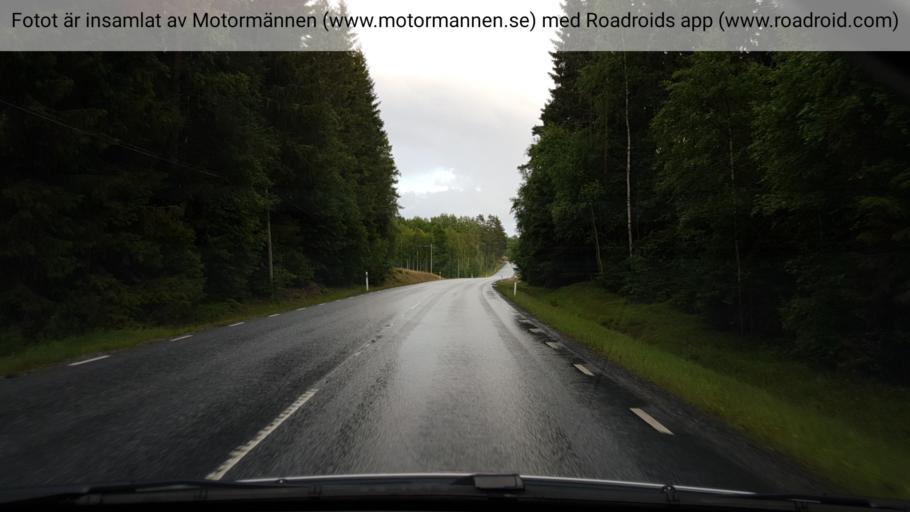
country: SE
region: OErebro
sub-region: Nora Kommun
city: As
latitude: 59.5438
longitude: 14.7798
